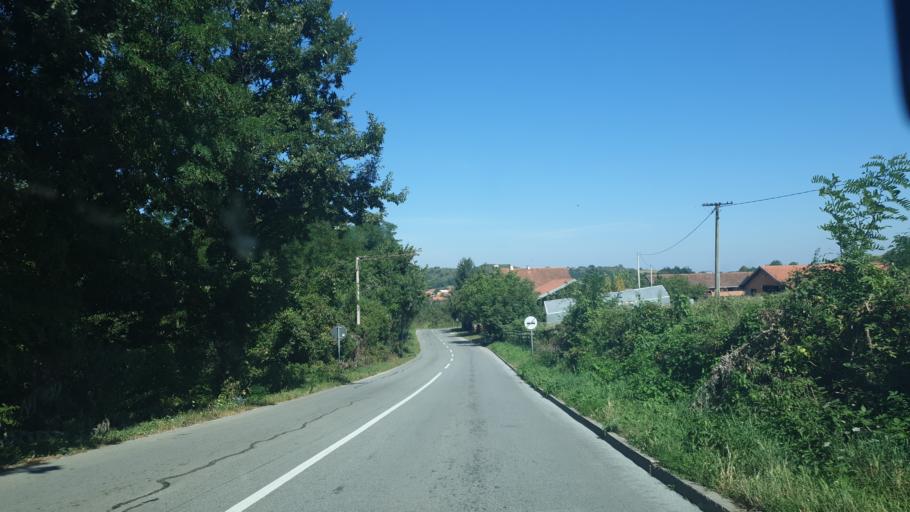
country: RS
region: Central Serbia
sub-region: Kolubarski Okrug
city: Mionica
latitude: 44.1825
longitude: 20.0331
